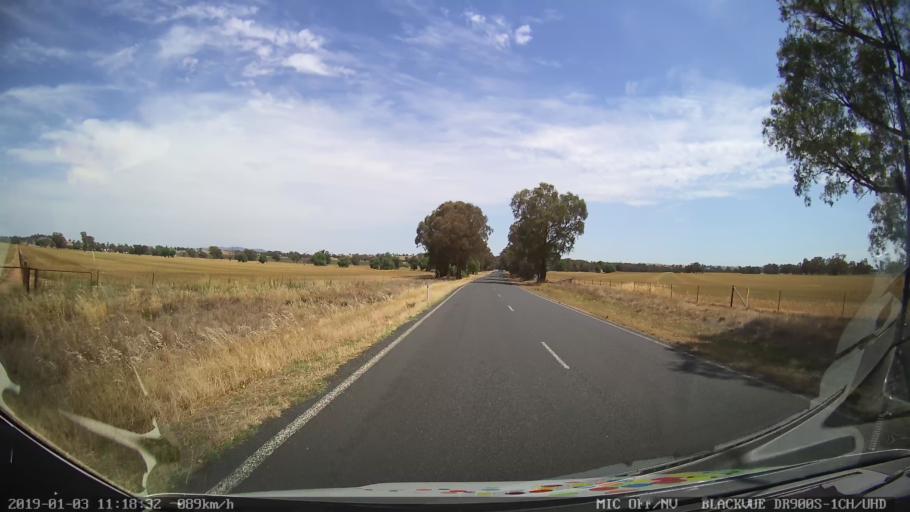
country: AU
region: New South Wales
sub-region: Young
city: Young
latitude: -34.1248
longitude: 148.2621
